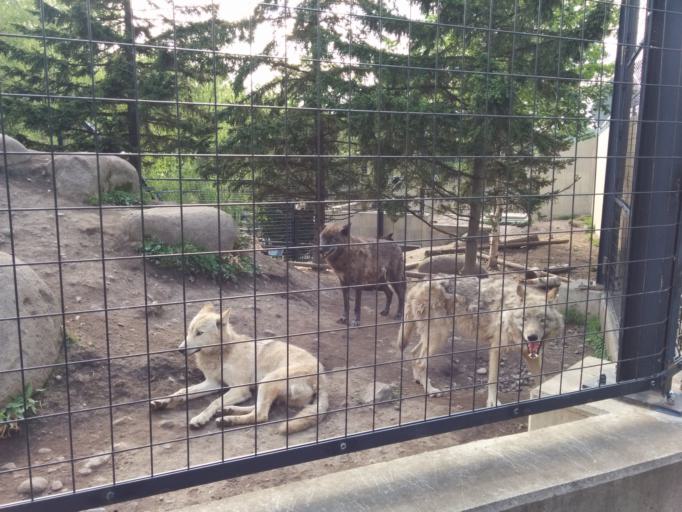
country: JP
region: Hokkaido
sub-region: Asahikawa-shi
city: Asahikawa
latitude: 43.7675
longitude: 142.4794
